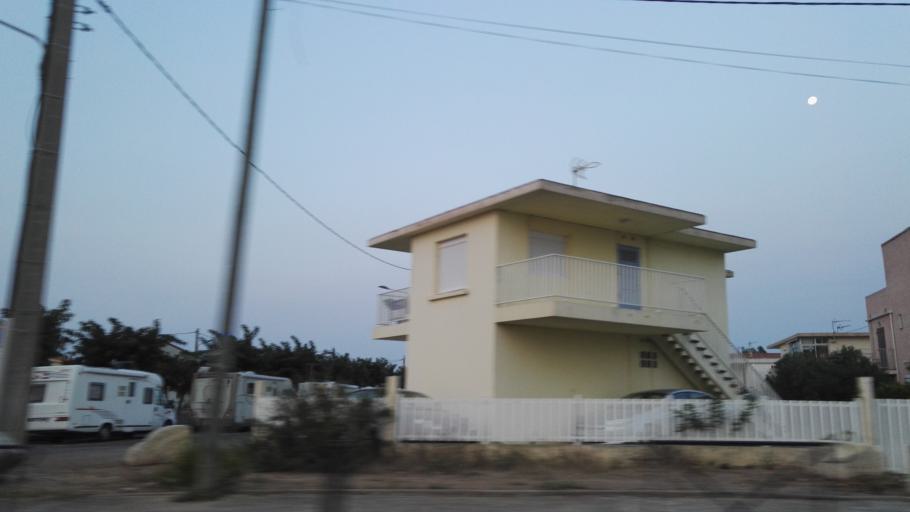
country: FR
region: Languedoc-Roussillon
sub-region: Departement de l'Herault
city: Marseillan
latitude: 43.3187
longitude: 3.5551
